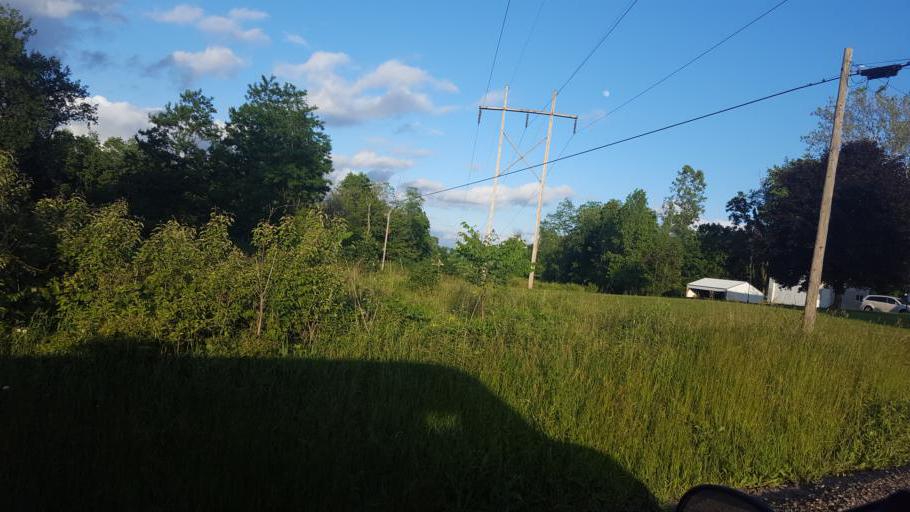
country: US
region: Ohio
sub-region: Knox County
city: Mount Vernon
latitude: 40.3813
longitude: -82.5649
